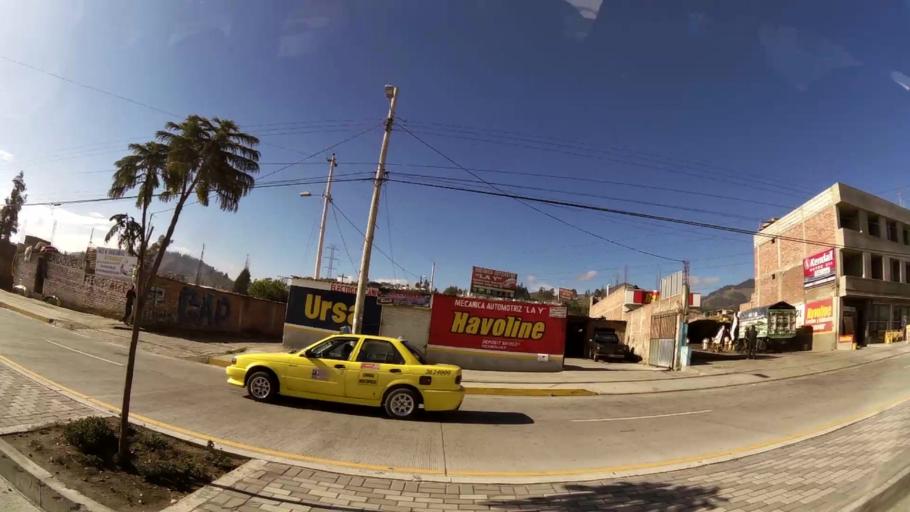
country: EC
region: Chimborazo
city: Riobamba
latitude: -1.6578
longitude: -78.6893
